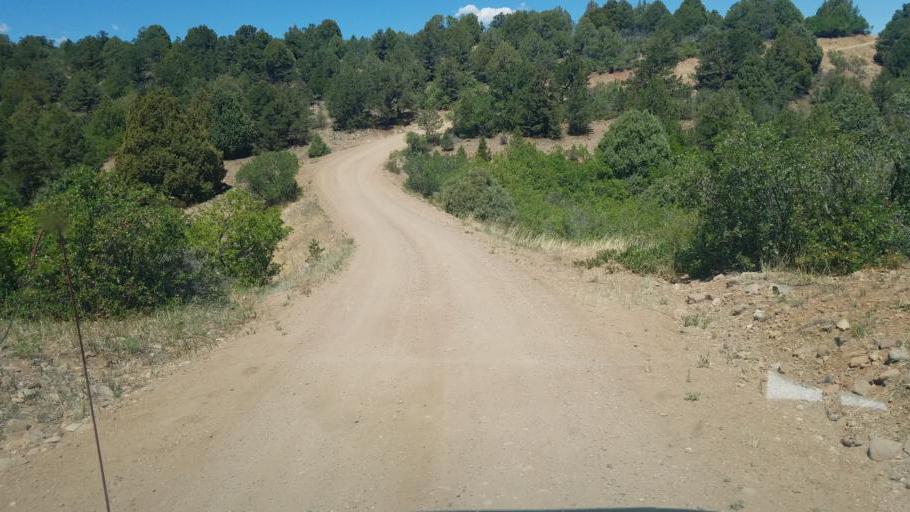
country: US
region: Colorado
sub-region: Custer County
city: Westcliffe
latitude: 38.3041
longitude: -105.6723
